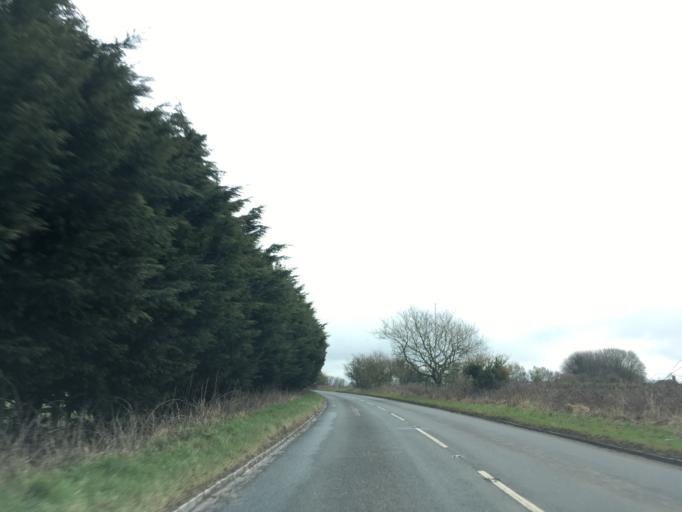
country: GB
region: England
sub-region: West Berkshire
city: Lambourn
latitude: 51.4894
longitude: -1.5707
